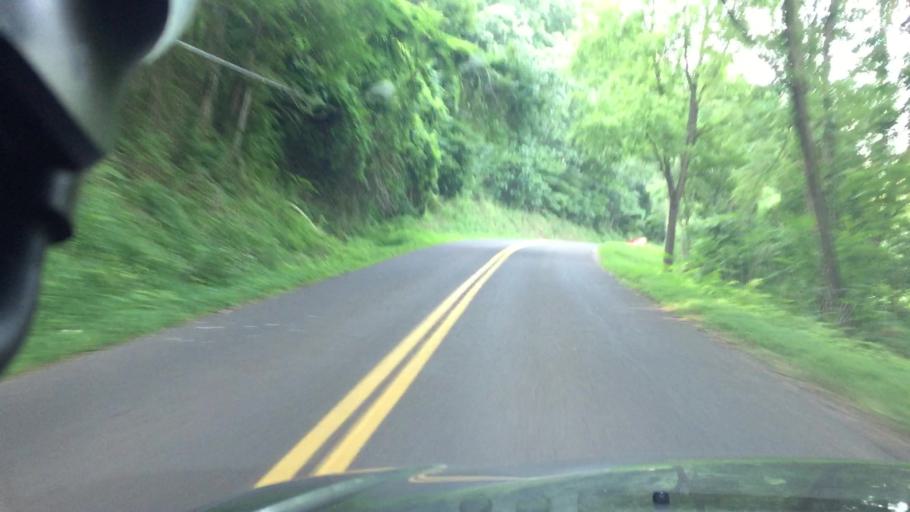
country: US
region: Pennsylvania
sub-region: Columbia County
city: Catawissa
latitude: 40.9573
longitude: -76.4460
